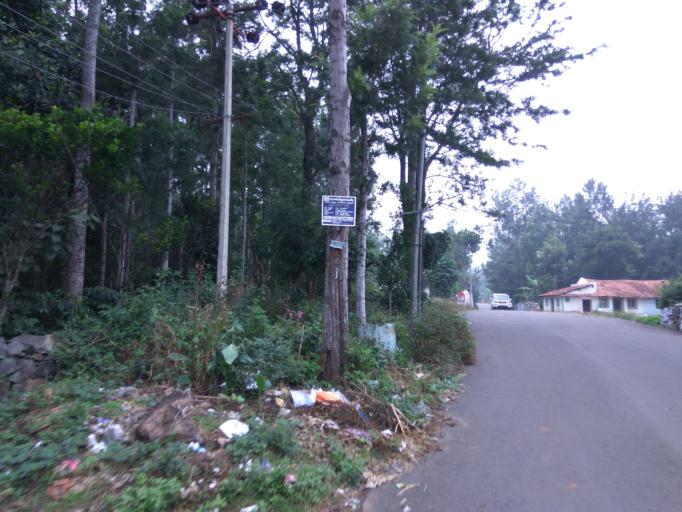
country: IN
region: Tamil Nadu
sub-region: Salem
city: Salem
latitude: 11.7685
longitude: 78.2376
